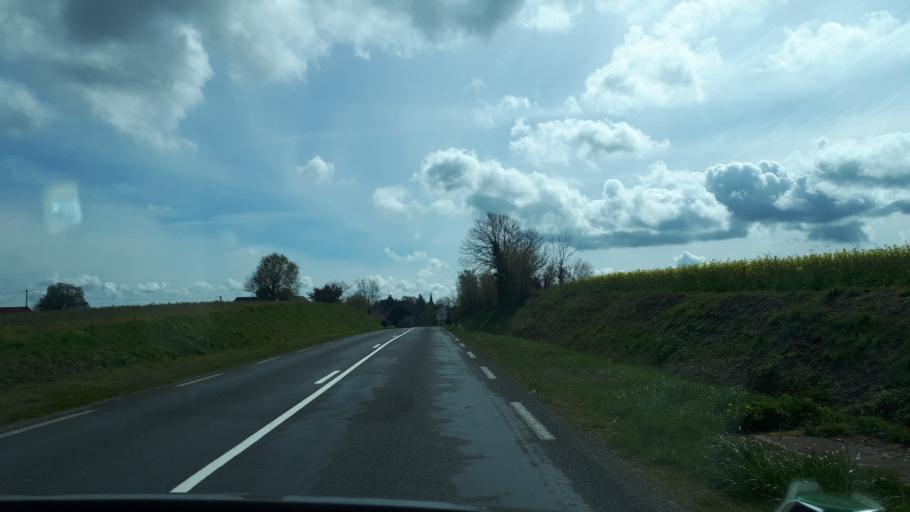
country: FR
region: Pays de la Loire
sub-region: Departement de la Sarthe
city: Le Grand-Luce
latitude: 47.8690
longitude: 0.4550
